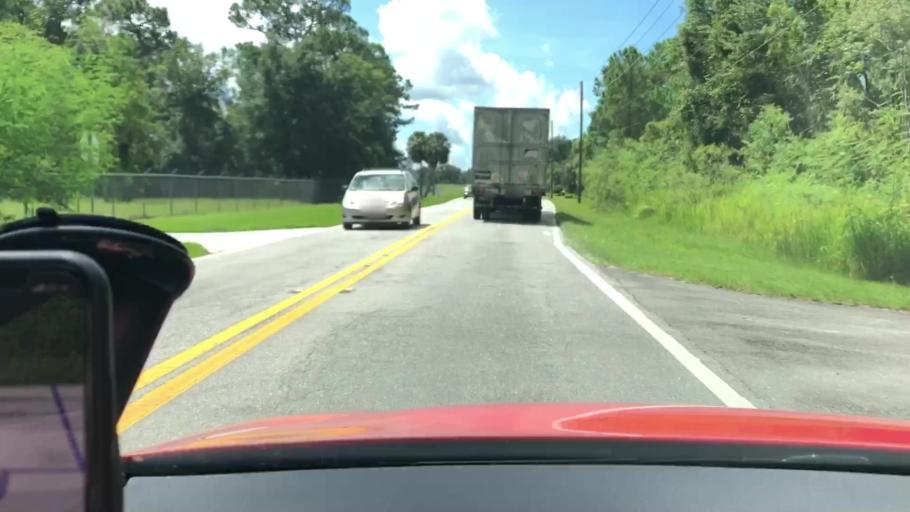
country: US
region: Florida
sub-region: Lake County
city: Eustis
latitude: 28.8566
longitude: -81.6529
